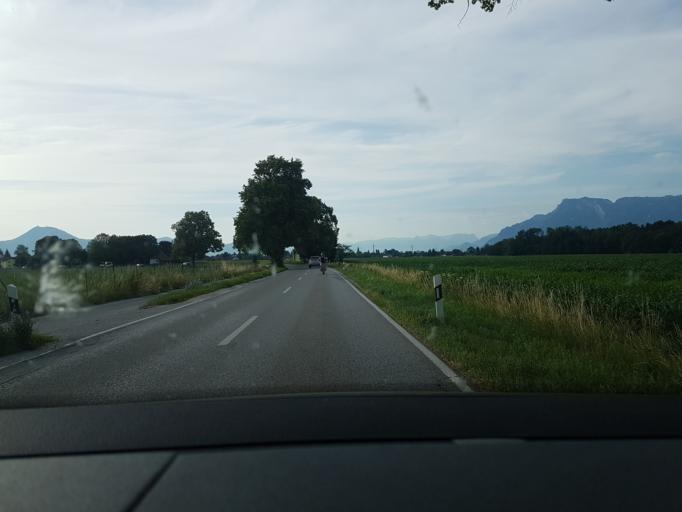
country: DE
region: Bavaria
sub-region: Upper Bavaria
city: Ainring
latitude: 47.8444
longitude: 12.9493
